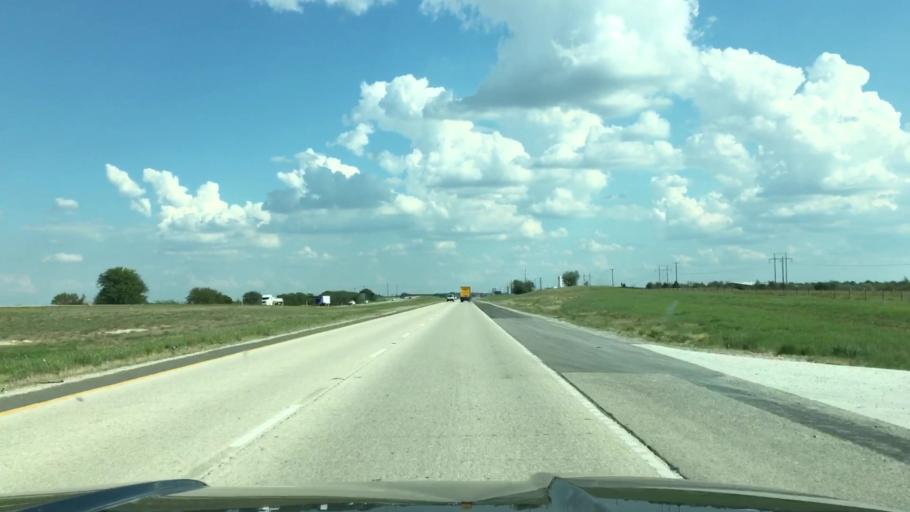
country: US
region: Texas
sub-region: Wise County
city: Decatur
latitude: 33.1856
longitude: -97.5528
